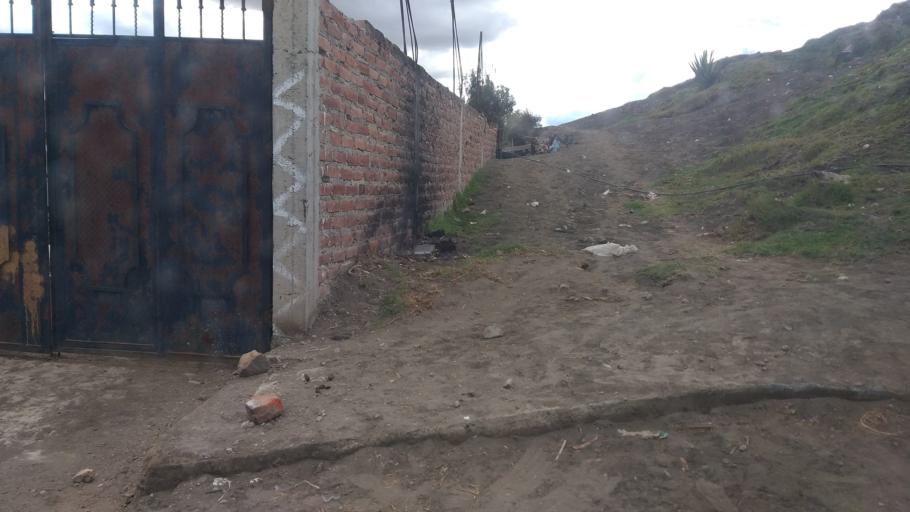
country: EC
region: Chimborazo
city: Riobamba
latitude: -1.6891
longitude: -78.6281
